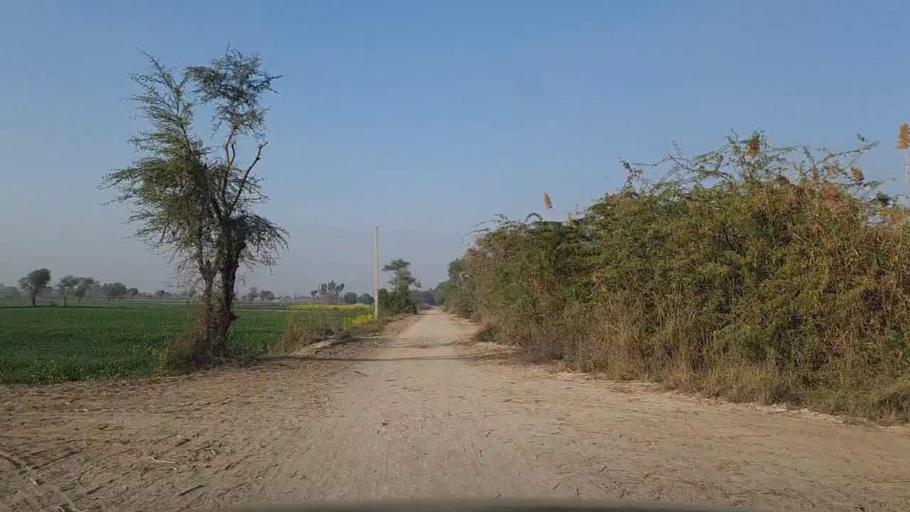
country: PK
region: Sindh
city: Daur
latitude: 26.4624
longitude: 68.4381
